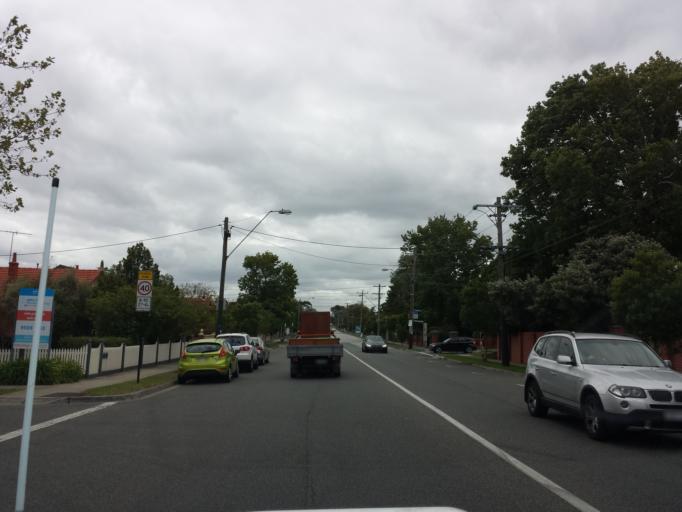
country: AU
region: Victoria
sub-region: Stonnington
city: Glen Iris
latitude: -37.8633
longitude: 145.0506
